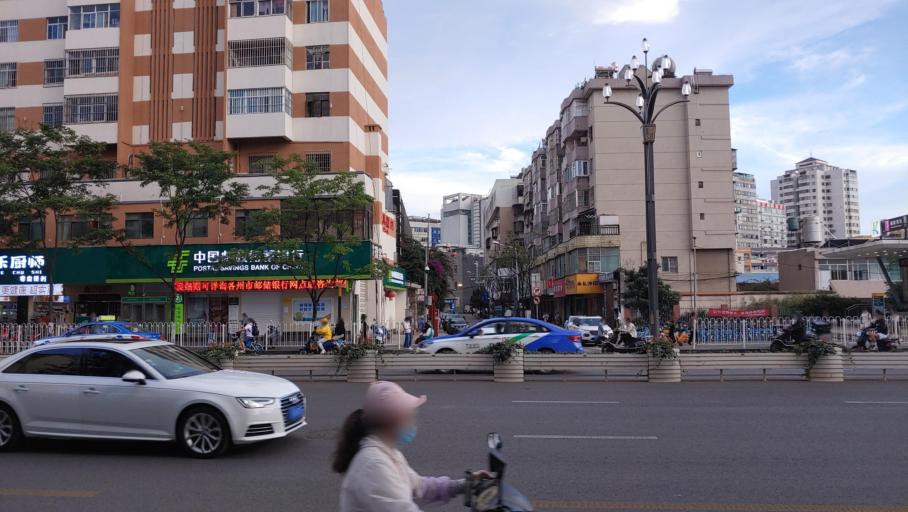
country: CN
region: Yunnan
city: Kunming
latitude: 25.0469
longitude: 102.6949
